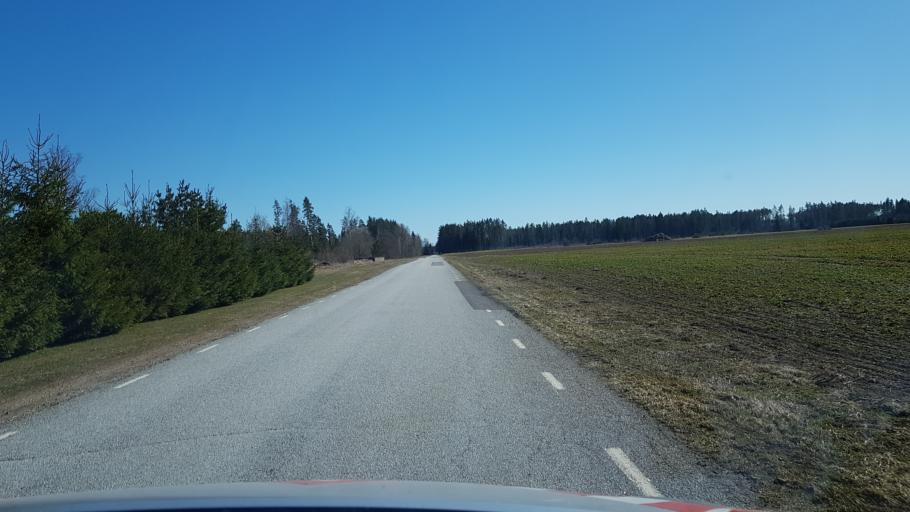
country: EE
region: Laeaene-Virumaa
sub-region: Viru-Nigula vald
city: Kunda
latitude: 59.3879
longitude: 26.5714
